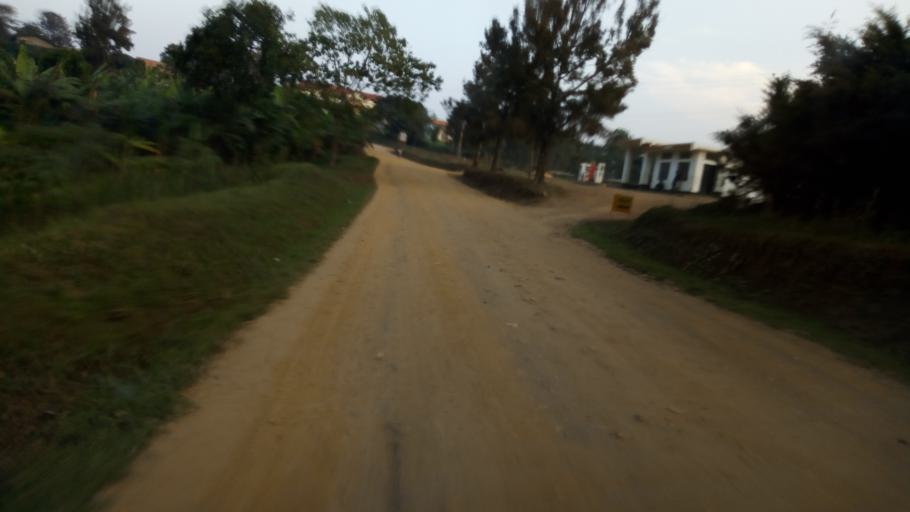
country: UG
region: Western Region
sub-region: Rukungiri District
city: Rukungiri
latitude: -0.7819
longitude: 29.9255
